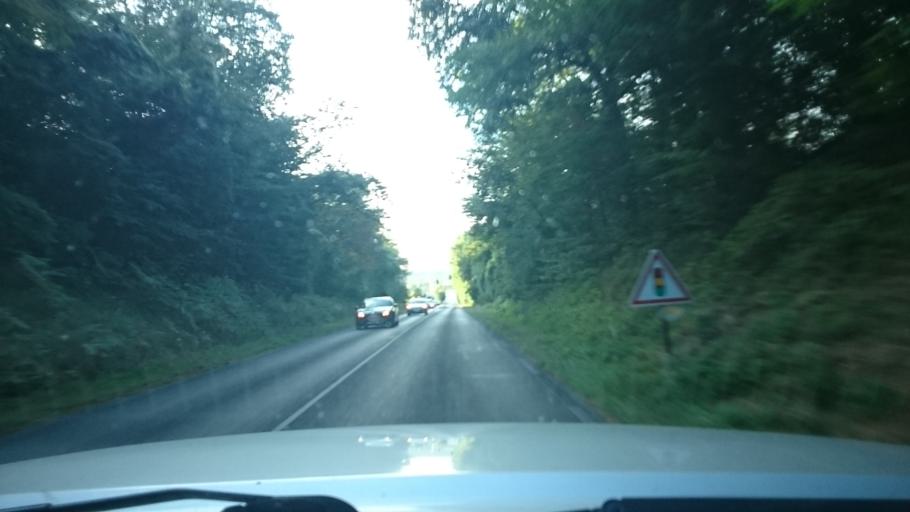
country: FR
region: Ile-de-France
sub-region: Departement de Seine-et-Marne
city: Samoreau
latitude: 48.4110
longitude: 2.7443
